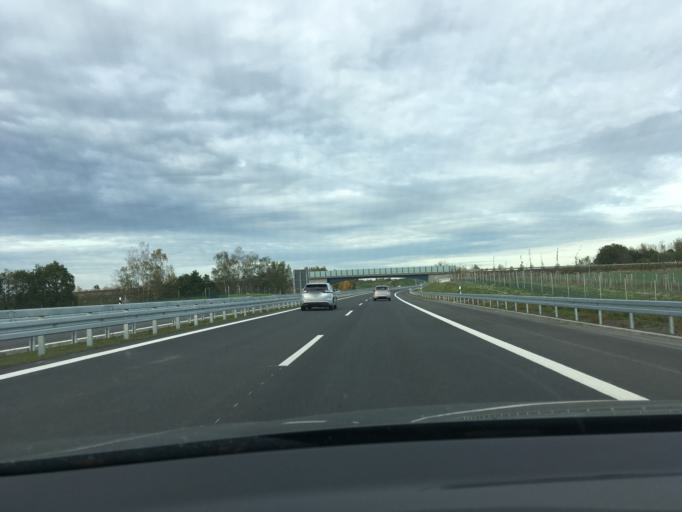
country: DE
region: Saxony
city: Borna
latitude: 51.1504
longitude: 12.5024
